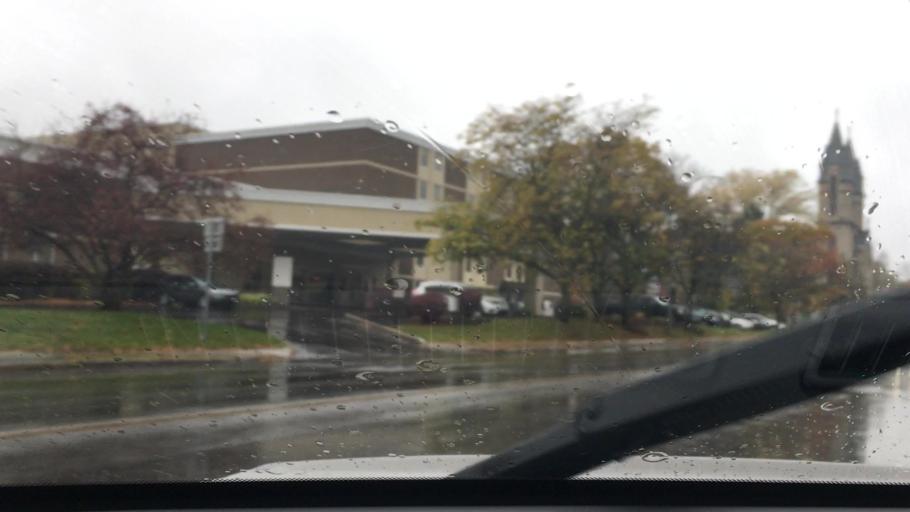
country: US
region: New York
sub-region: Cayuga County
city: Auburn
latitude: 42.9345
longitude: -76.5663
